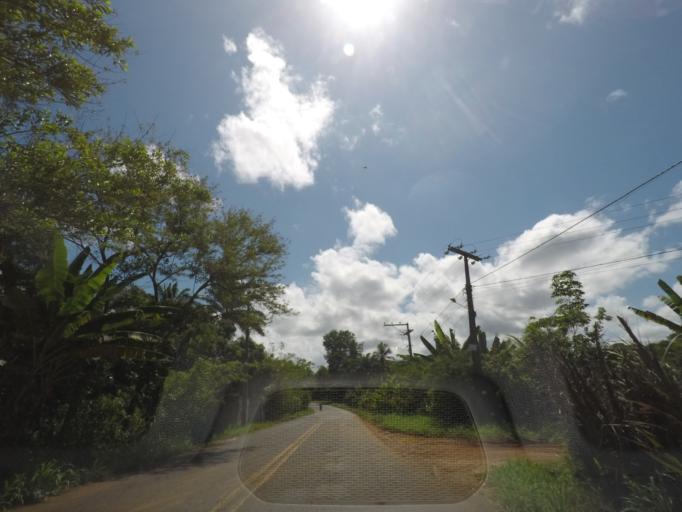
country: BR
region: Bahia
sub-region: Taperoa
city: Taperoa
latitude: -13.4949
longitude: -39.0949
